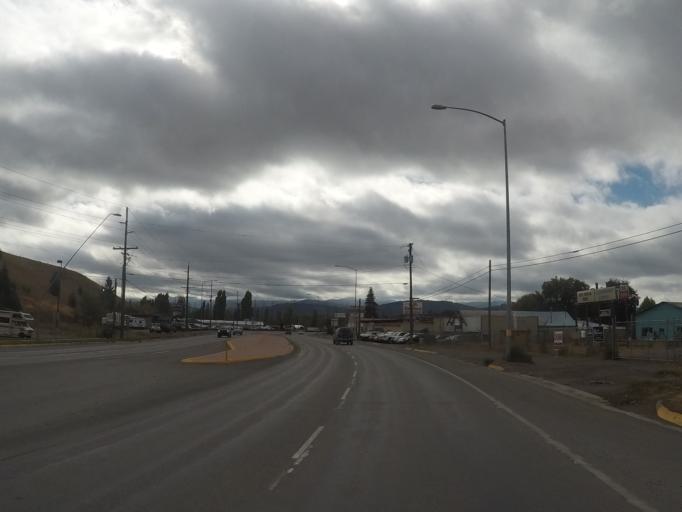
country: US
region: Montana
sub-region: Flathead County
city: Evergreen
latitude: 48.2094
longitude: -114.2927
